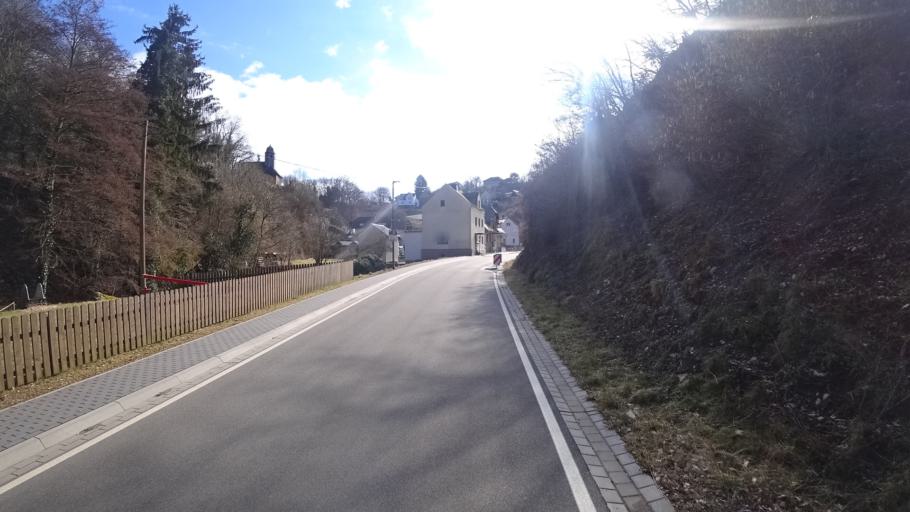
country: DE
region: Rheinland-Pfalz
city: Lierschied
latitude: 50.1586
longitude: 7.7581
